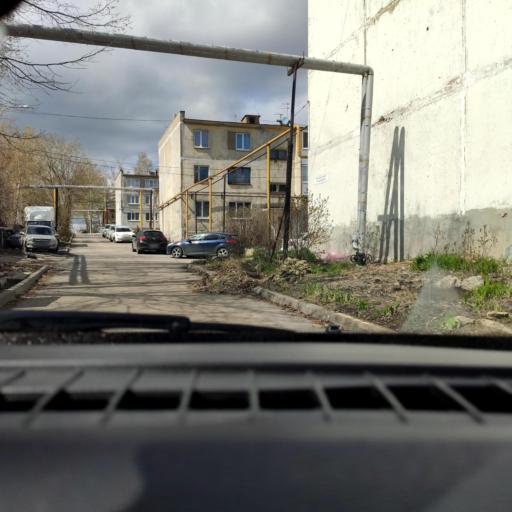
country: RU
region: Samara
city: Petra-Dubrava
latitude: 53.2880
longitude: 50.2432
